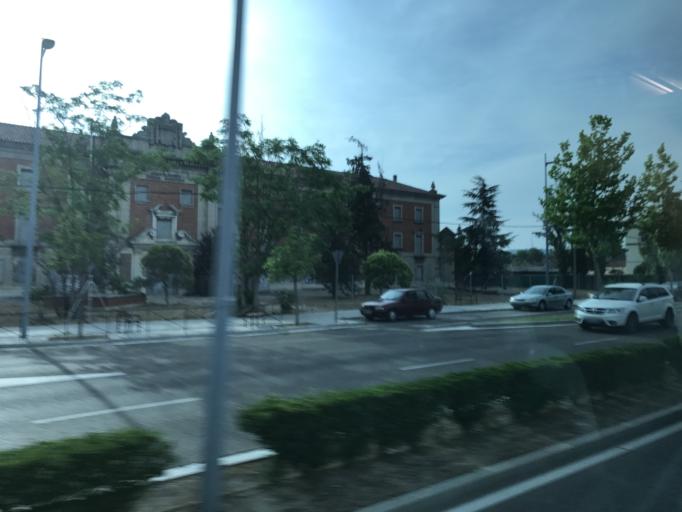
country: ES
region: Castille and Leon
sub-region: Provincia de Valladolid
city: Valladolid
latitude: 41.6363
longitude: -4.7298
